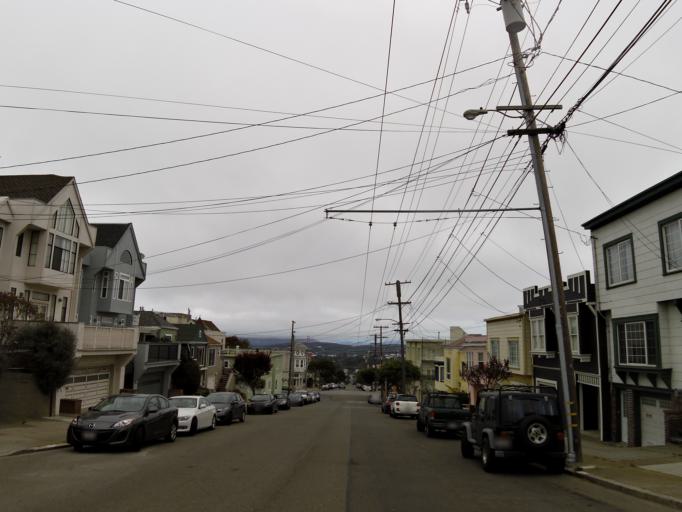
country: US
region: California
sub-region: San Mateo County
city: Daly City
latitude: 37.7537
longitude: -122.4667
